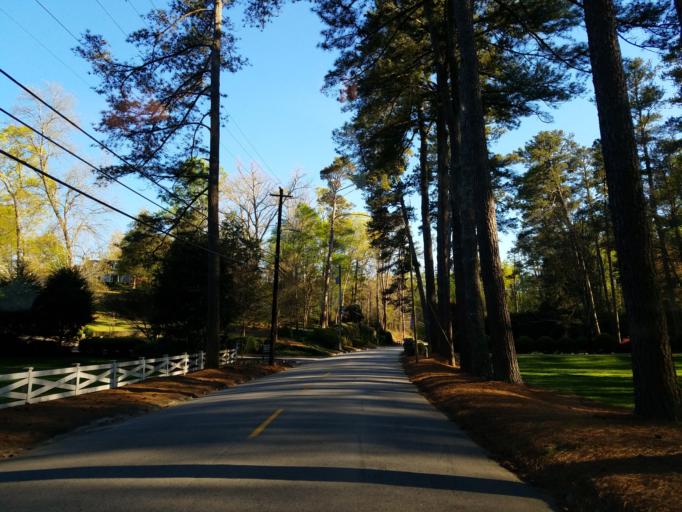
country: US
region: Georgia
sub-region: Cobb County
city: Vinings
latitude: 33.8433
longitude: -84.4407
